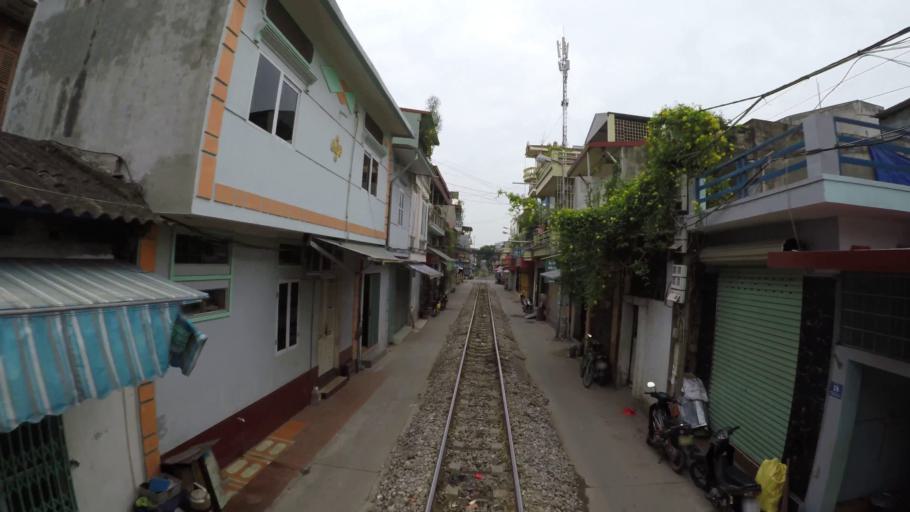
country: VN
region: Hai Phong
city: Haiphong
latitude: 20.8610
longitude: 106.6626
